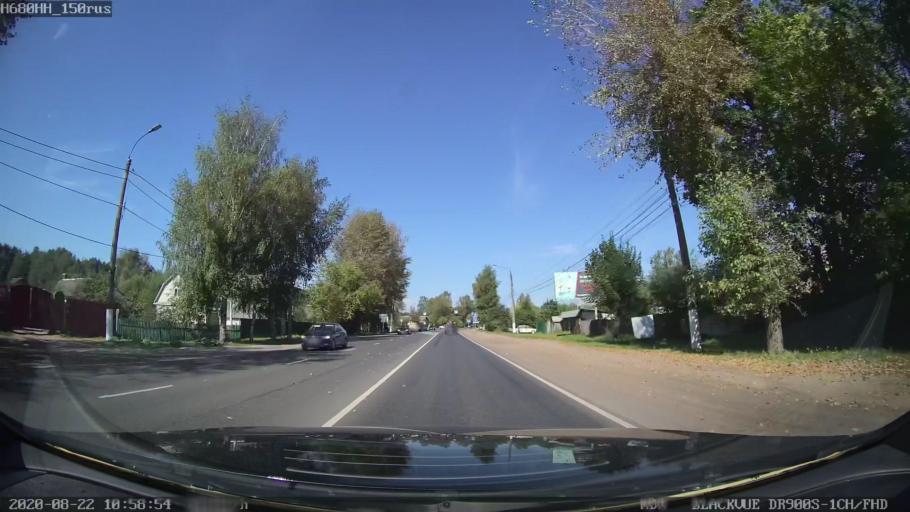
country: RU
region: Tverskaya
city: Tver
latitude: 56.8209
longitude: 35.9782
